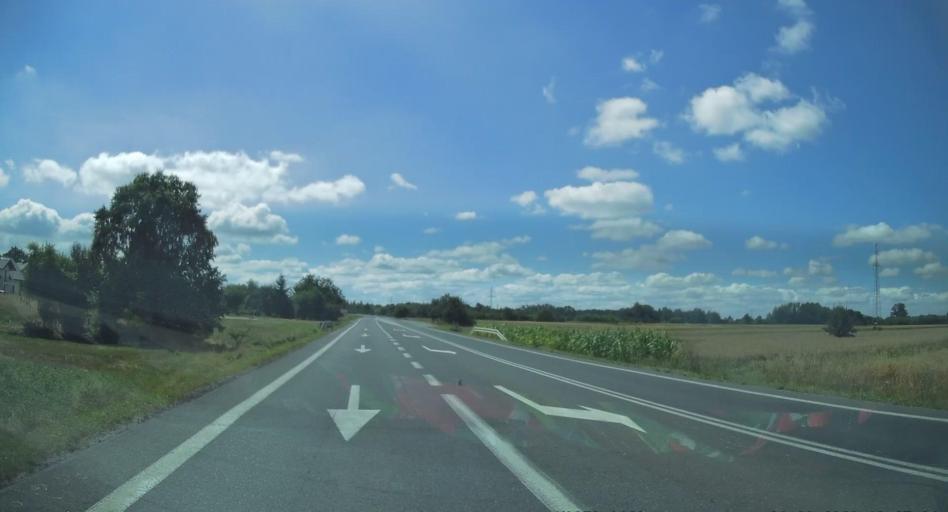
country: PL
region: Subcarpathian Voivodeship
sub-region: Powiat debicki
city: Brzeznica
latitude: 50.1423
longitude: 21.4854
